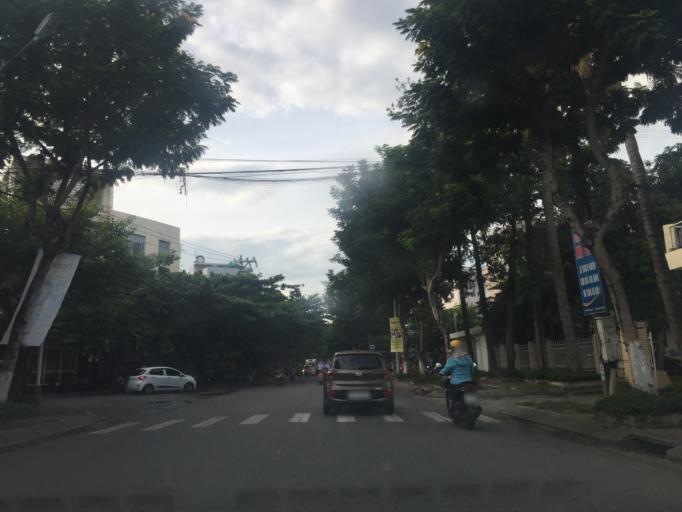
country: VN
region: Da Nang
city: Da Nang
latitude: 16.0794
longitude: 108.2116
